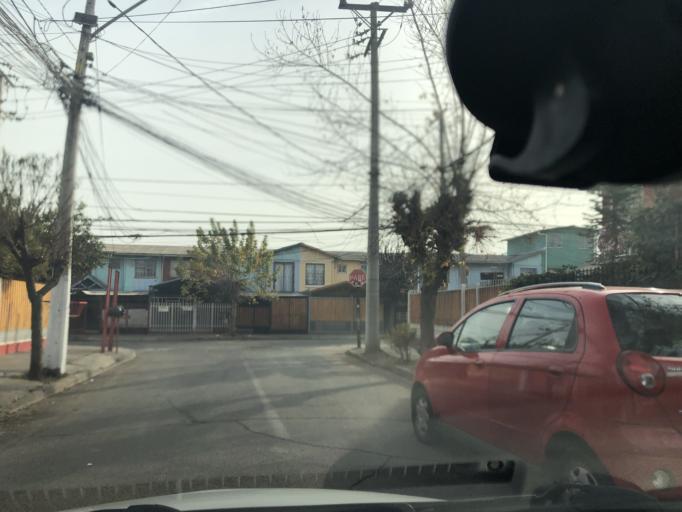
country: CL
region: Santiago Metropolitan
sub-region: Provincia de Cordillera
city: Puente Alto
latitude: -33.5803
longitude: -70.5549
